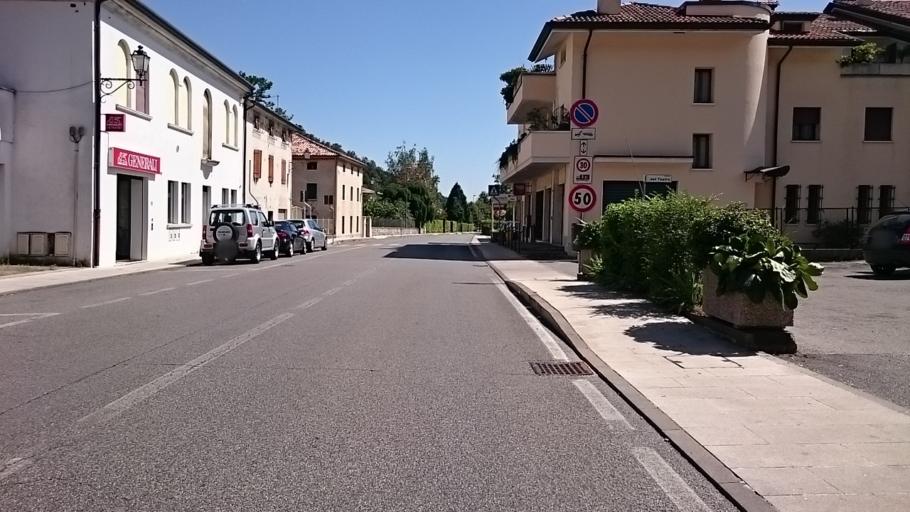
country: IT
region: Veneto
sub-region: Provincia di Treviso
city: Follina
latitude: 45.9512
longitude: 12.1198
